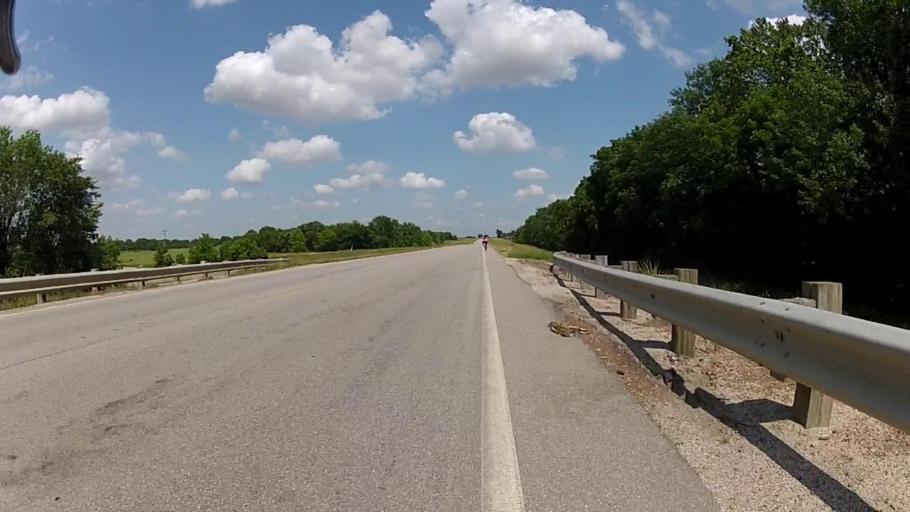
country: US
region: Kansas
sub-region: Labette County
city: Oswego
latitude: 37.1938
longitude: -95.1915
